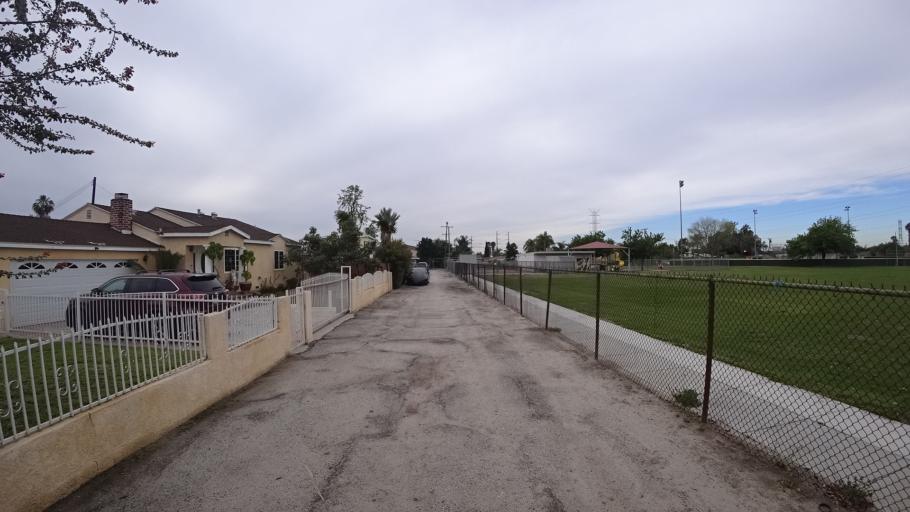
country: US
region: California
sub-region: Los Angeles County
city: West Puente Valley
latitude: 34.0722
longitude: -117.9907
